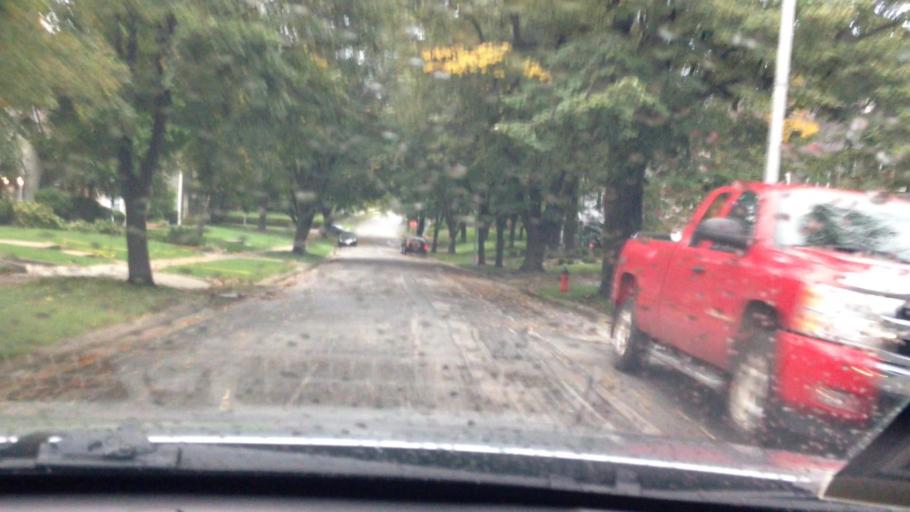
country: US
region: Kansas
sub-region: Johnson County
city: Mission Hills
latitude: 39.0015
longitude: -94.5980
